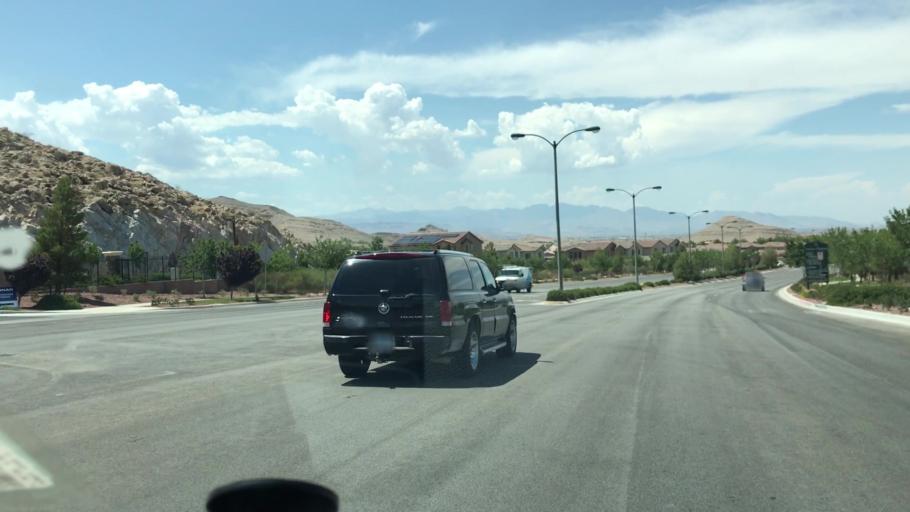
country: US
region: Nevada
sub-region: Clark County
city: Enterprise
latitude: 35.9630
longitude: -115.1856
